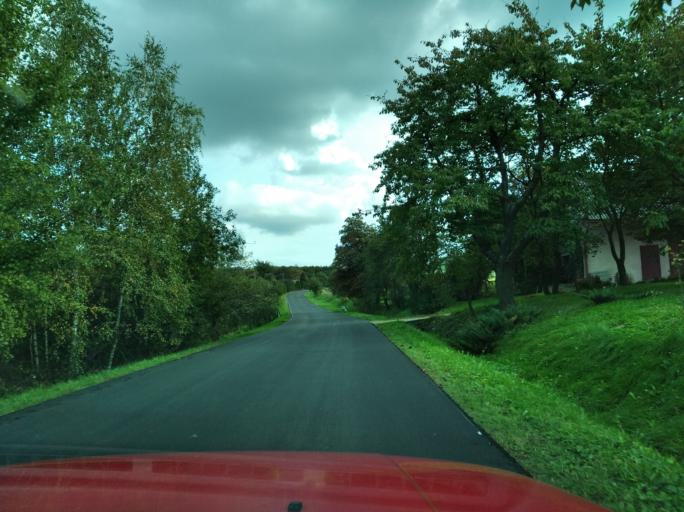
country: PL
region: Subcarpathian Voivodeship
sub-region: Powiat rzeszowski
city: Straszydle
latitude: 49.9344
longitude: 21.9826
